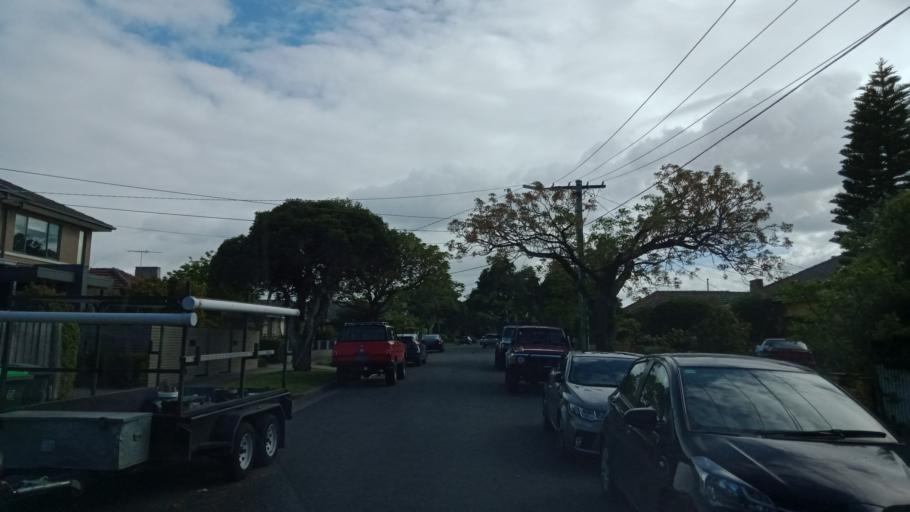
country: AU
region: Victoria
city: McKinnon
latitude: -37.9222
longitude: 145.0517
